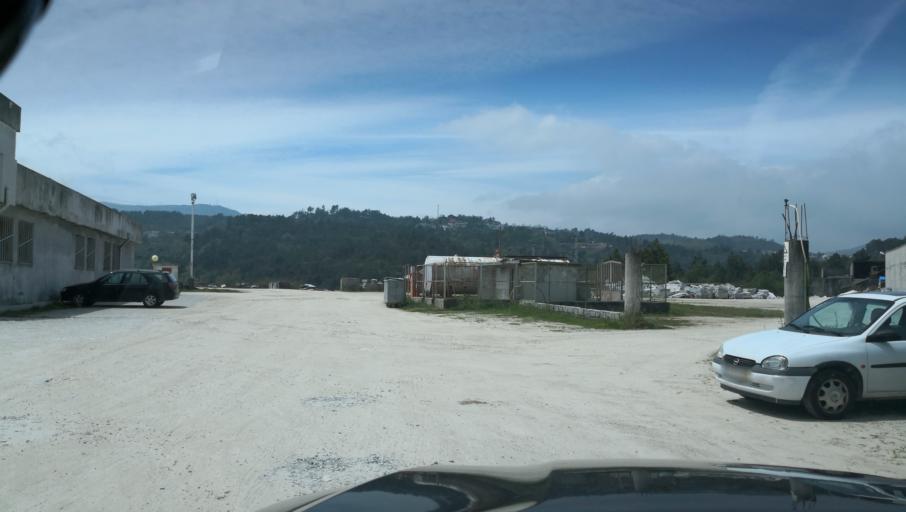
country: PT
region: Vila Real
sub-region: Vila Real
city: Vila Real
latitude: 41.2752
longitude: -7.7968
